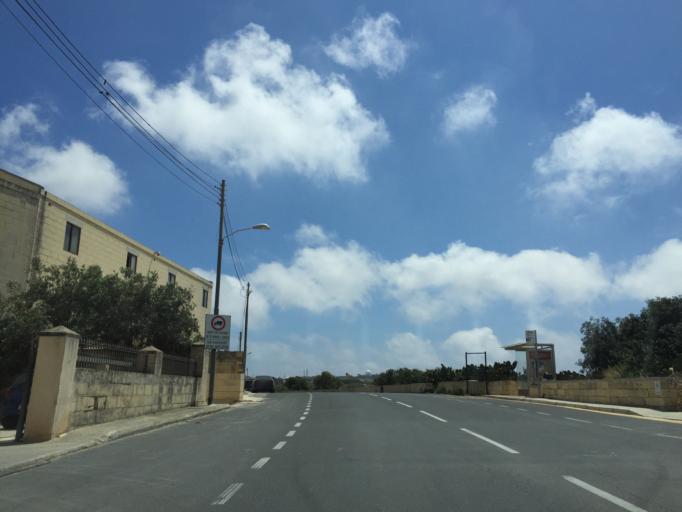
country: MT
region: Dingli
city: Dingli
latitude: 35.8702
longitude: 14.3911
